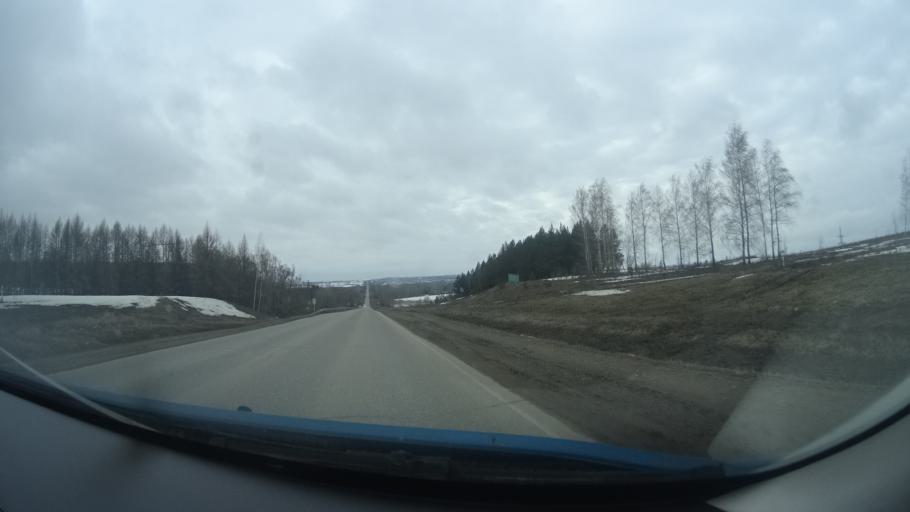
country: RU
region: Bashkortostan
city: Birsk
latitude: 55.4869
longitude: 55.5993
